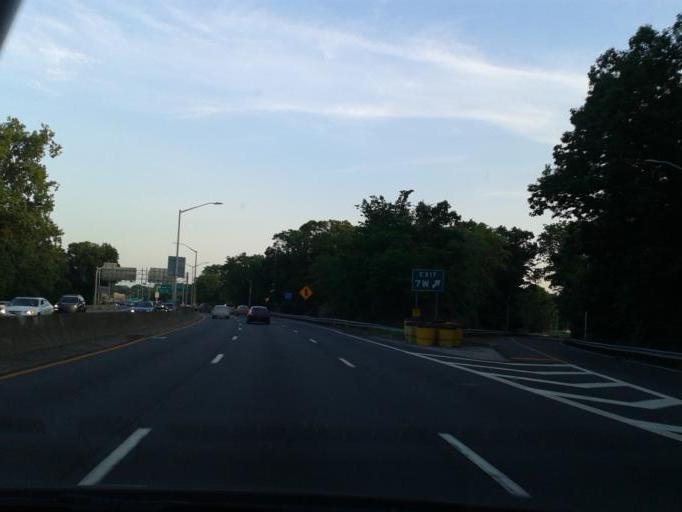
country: US
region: New York
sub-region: Bronx
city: The Bronx
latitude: 40.8585
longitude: -73.8727
